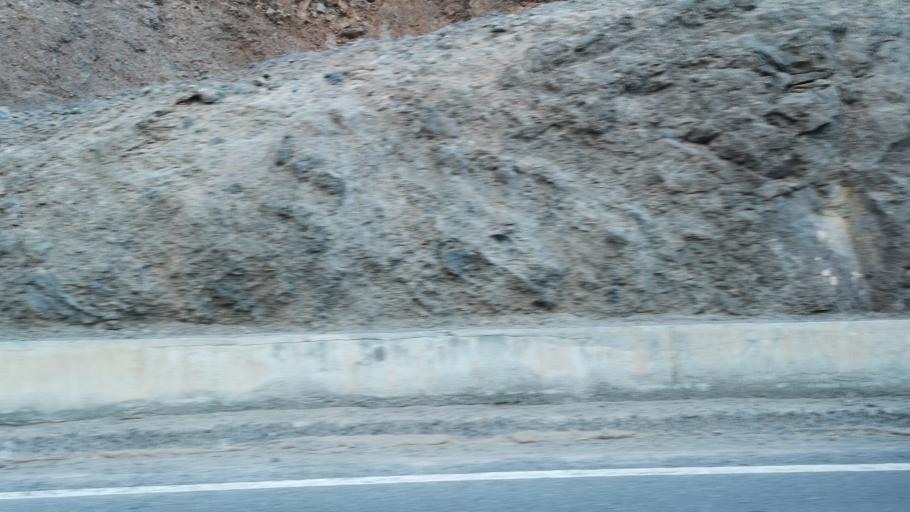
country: ES
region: Canary Islands
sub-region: Provincia de Santa Cruz de Tenerife
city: Alajero
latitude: 28.0340
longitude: -17.2026
